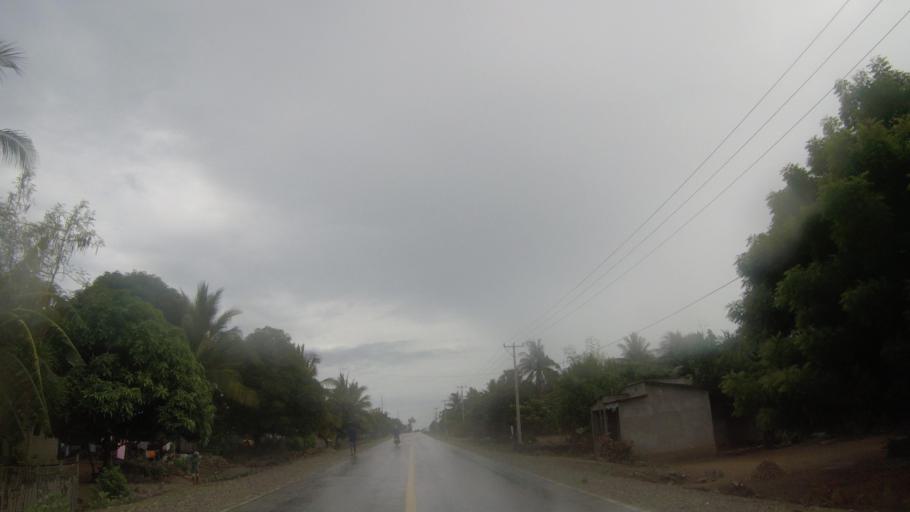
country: TL
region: Lautem
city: Lospalos
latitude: -8.3742
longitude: 126.8745
